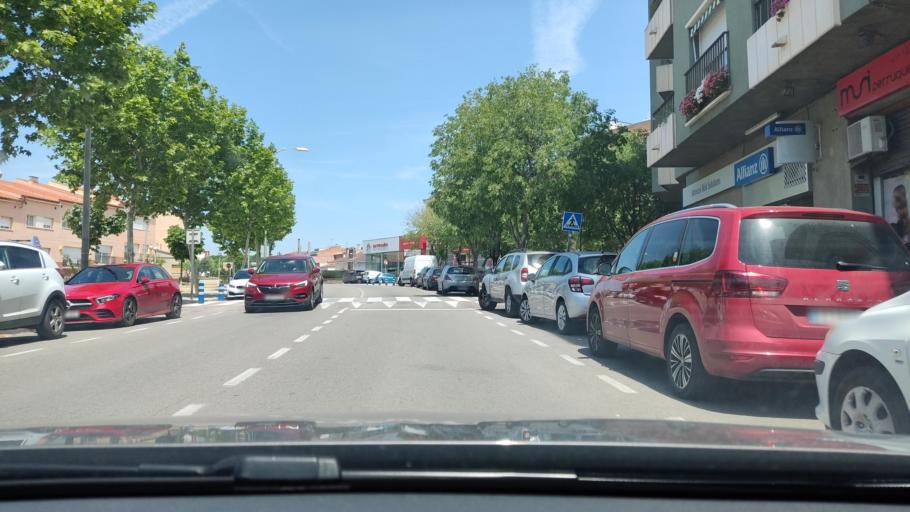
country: ES
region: Catalonia
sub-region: Provincia de Barcelona
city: Sant Sadurni d'Anoia
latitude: 41.4257
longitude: 1.7811
